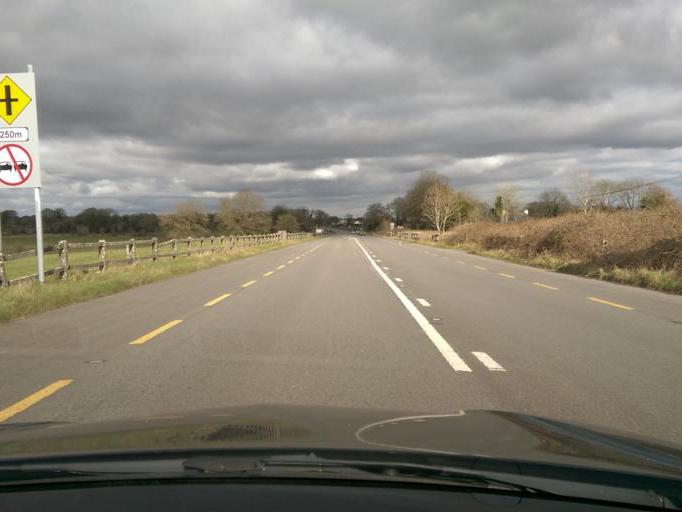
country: IE
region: Connaught
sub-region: County Galway
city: Ballinasloe
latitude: 53.3439
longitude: -8.0968
